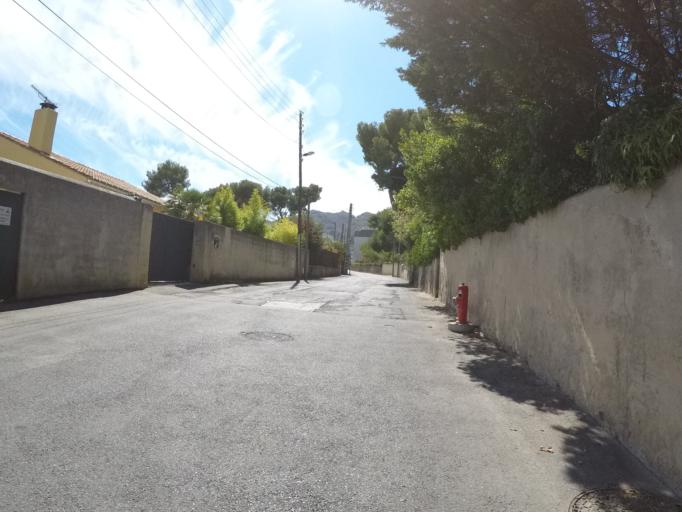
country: FR
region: Provence-Alpes-Cote d'Azur
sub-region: Departement des Bouches-du-Rhone
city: Marseille 09
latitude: 43.2365
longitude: 5.4038
